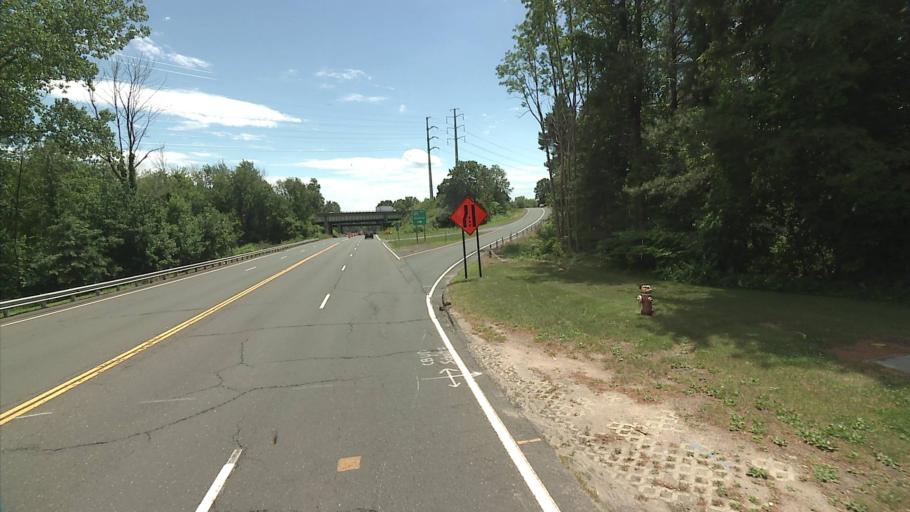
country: US
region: Connecticut
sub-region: New Haven County
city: Middlebury
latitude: 41.5376
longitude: -73.0876
